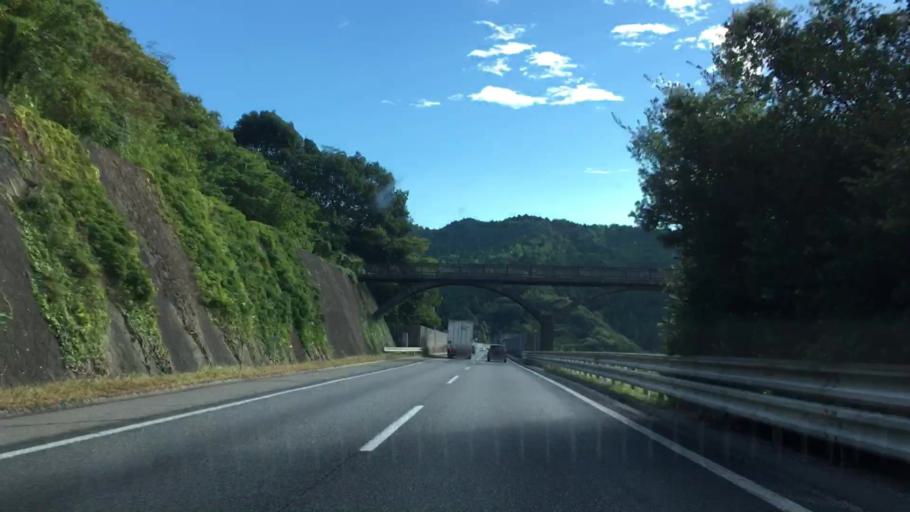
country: JP
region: Yamaguchi
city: Iwakuni
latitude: 34.1599
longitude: 132.1528
